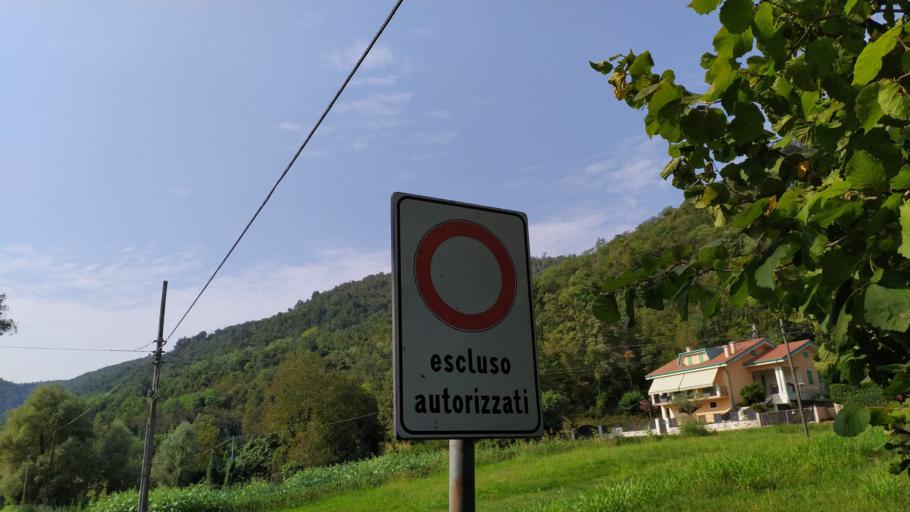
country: IT
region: Veneto
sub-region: Provincia di Vicenza
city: Arcugnano-Torri
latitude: 45.4697
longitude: 11.5400
